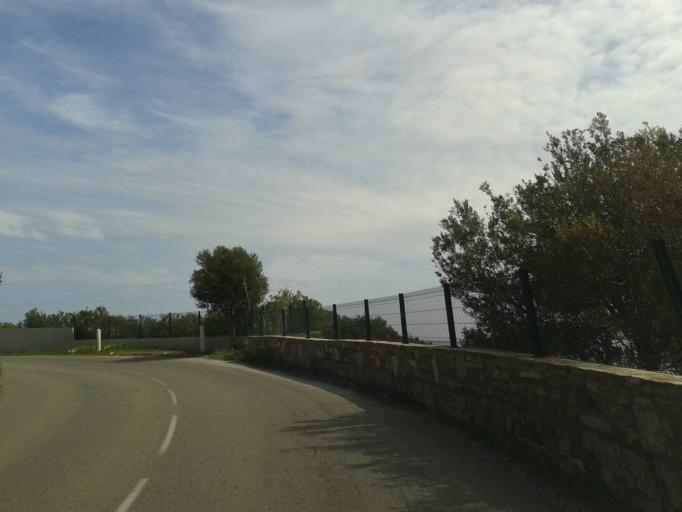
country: FR
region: Corsica
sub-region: Departement de la Haute-Corse
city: Brando
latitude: 42.7812
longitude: 9.4806
